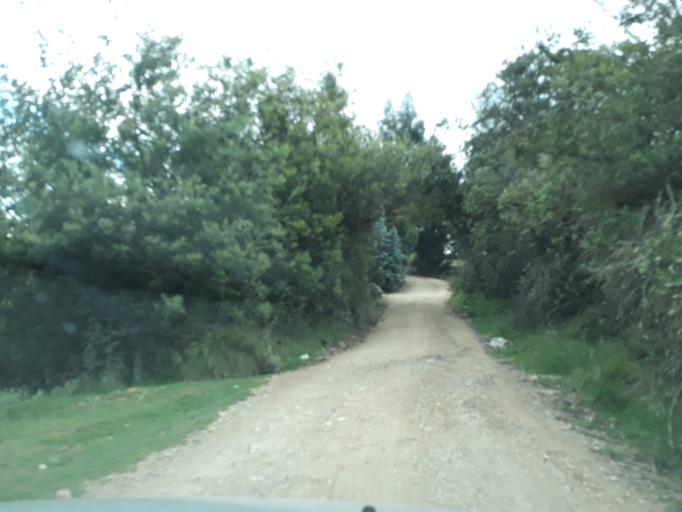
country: CO
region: Cundinamarca
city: Lenguazaque
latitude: 5.2780
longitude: -73.6834
